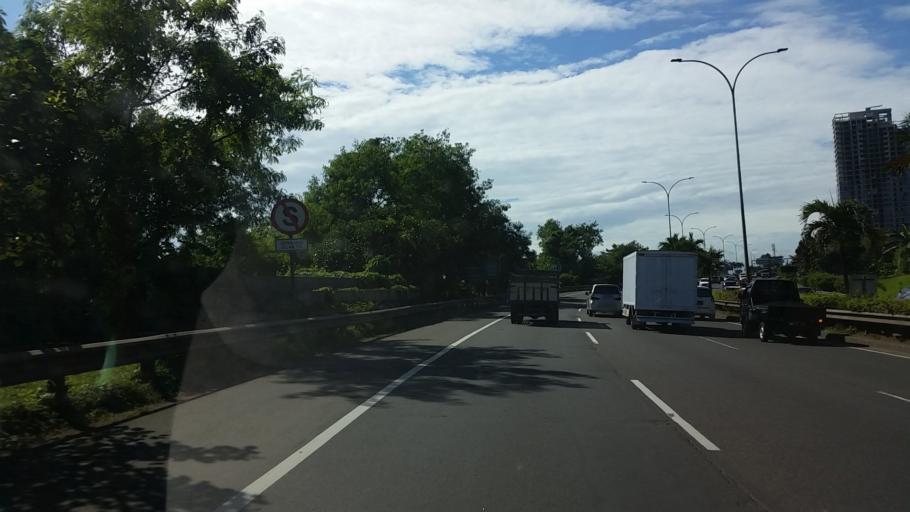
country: ID
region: Banten
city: South Tangerang
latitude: -6.2688
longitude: 106.7684
